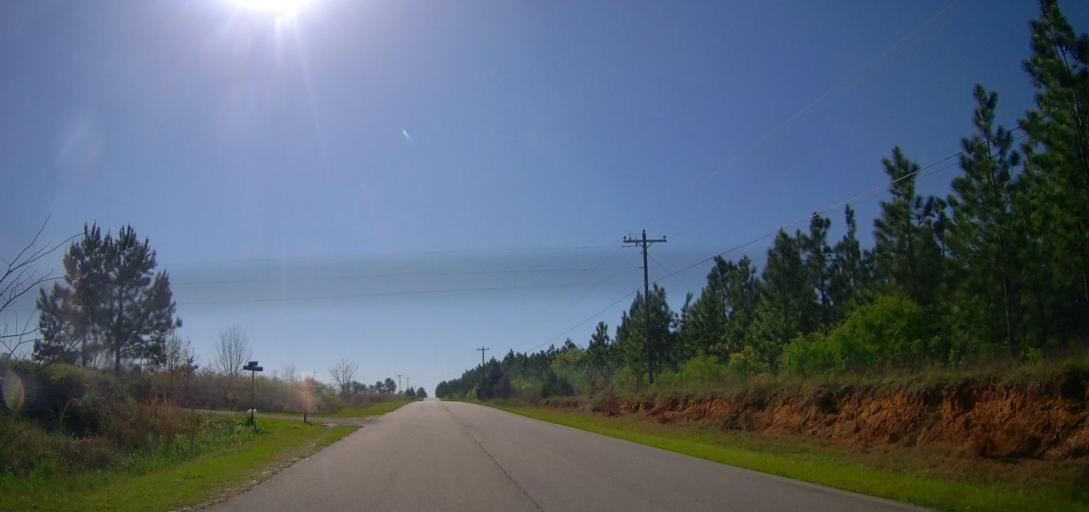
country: US
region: Georgia
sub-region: Pulaski County
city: Hawkinsville
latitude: 32.2404
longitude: -83.5184
